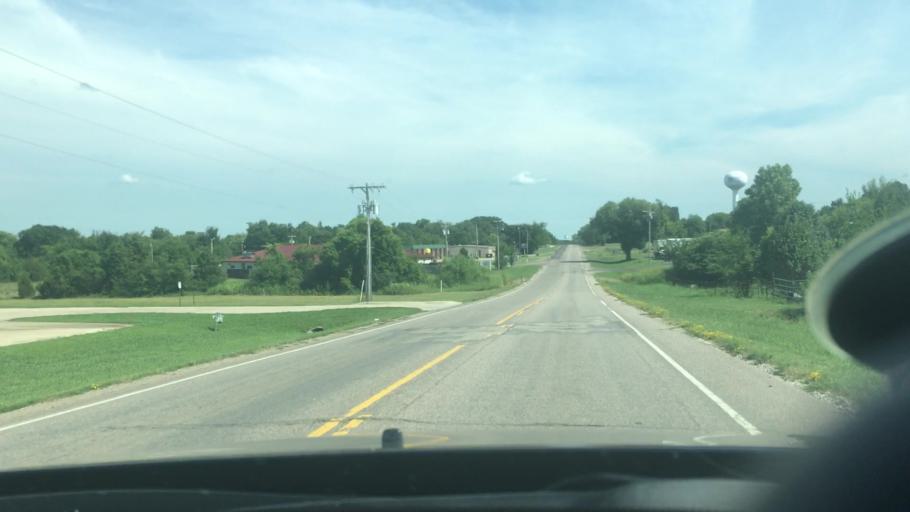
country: US
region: Oklahoma
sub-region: Seminole County
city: Seminole
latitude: 35.2406
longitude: -96.6959
